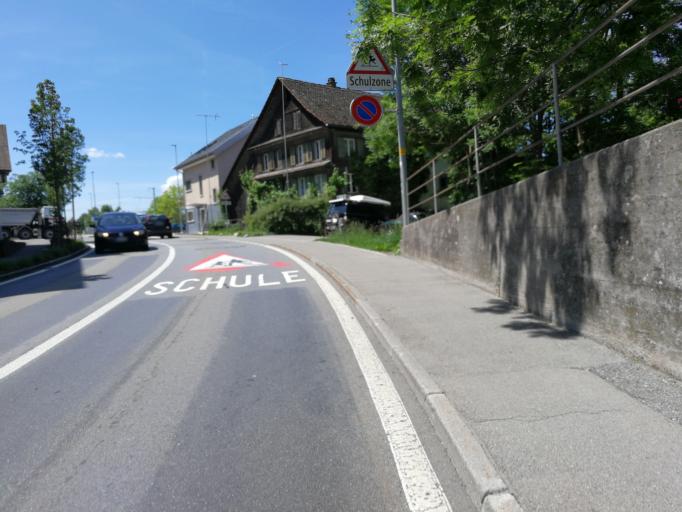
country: CH
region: Schwyz
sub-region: Bezirk Hoefe
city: Feusisberg
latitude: 47.1975
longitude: 8.7362
